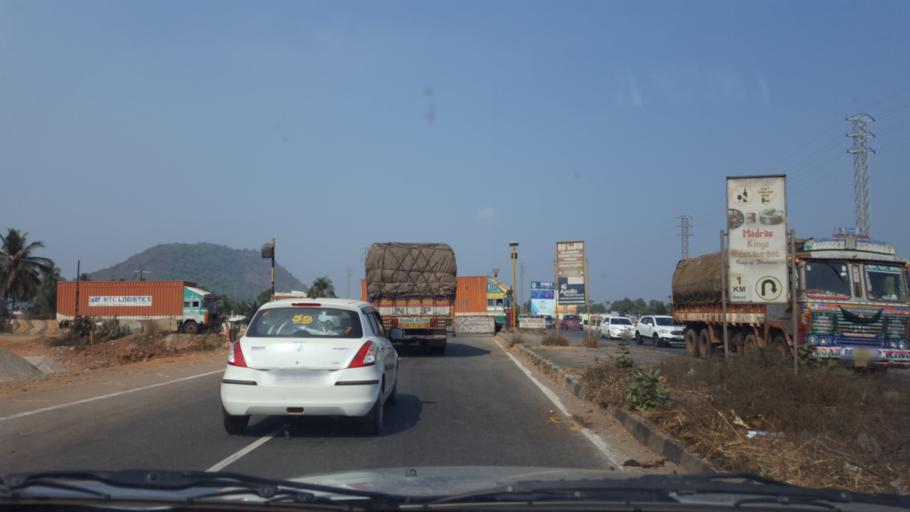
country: IN
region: Andhra Pradesh
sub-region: Vishakhapatnam
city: Bhimunipatnam
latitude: 17.8985
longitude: 83.3842
